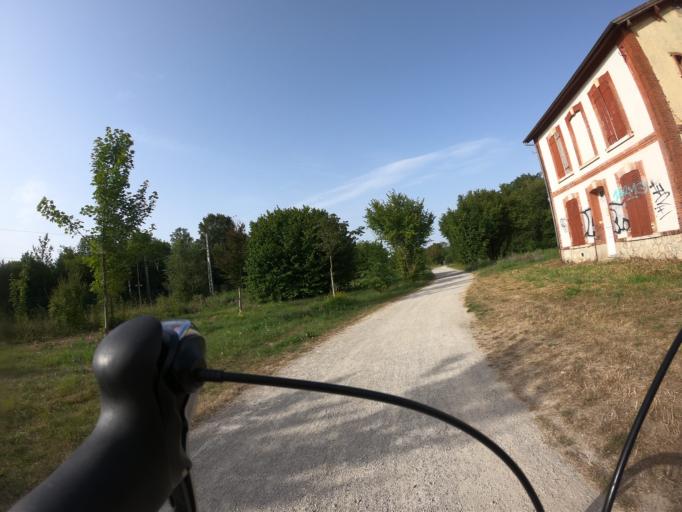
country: FR
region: Lower Normandy
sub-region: Departement de l'Orne
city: Conde-sur-Huisne
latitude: 48.3849
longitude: 0.8498
